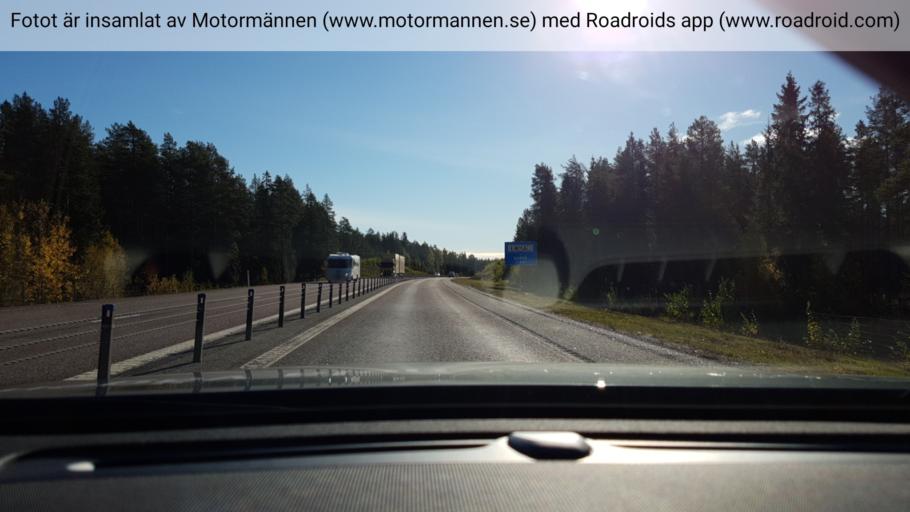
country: SE
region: Vaesterbotten
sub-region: Skelleftea Kommun
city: Burea
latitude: 64.6399
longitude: 21.1641
